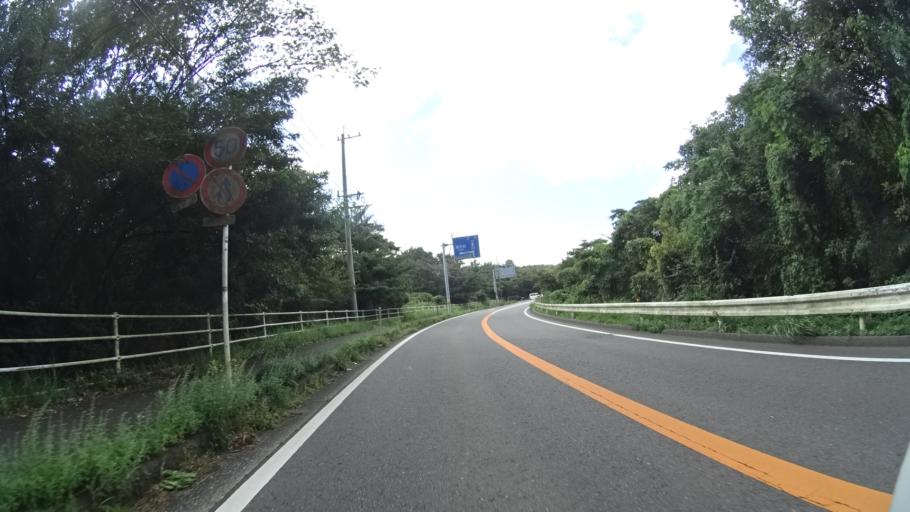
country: JP
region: Oita
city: Beppu
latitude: 33.3455
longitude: 131.4288
